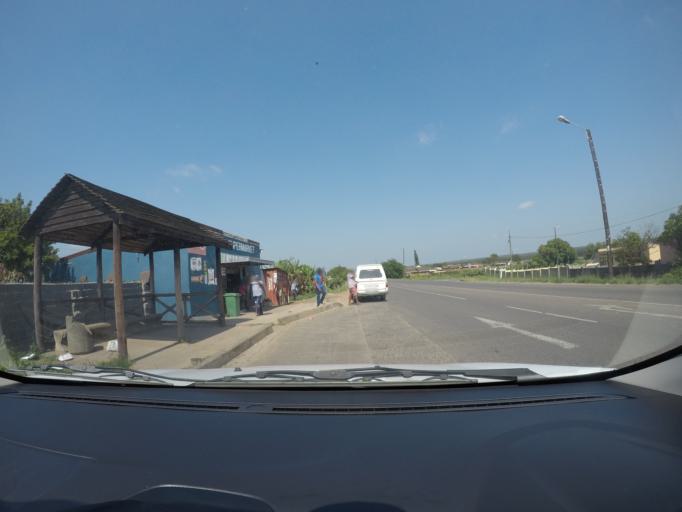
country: ZA
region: KwaZulu-Natal
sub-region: uThungulu District Municipality
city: eSikhawini
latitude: -28.8927
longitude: 31.8858
